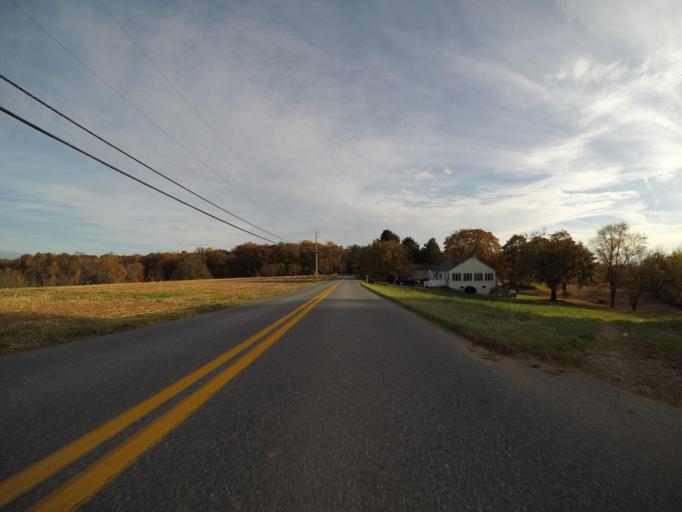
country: US
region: Maryland
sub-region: Baltimore County
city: Reisterstown
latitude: 39.5346
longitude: -76.7845
